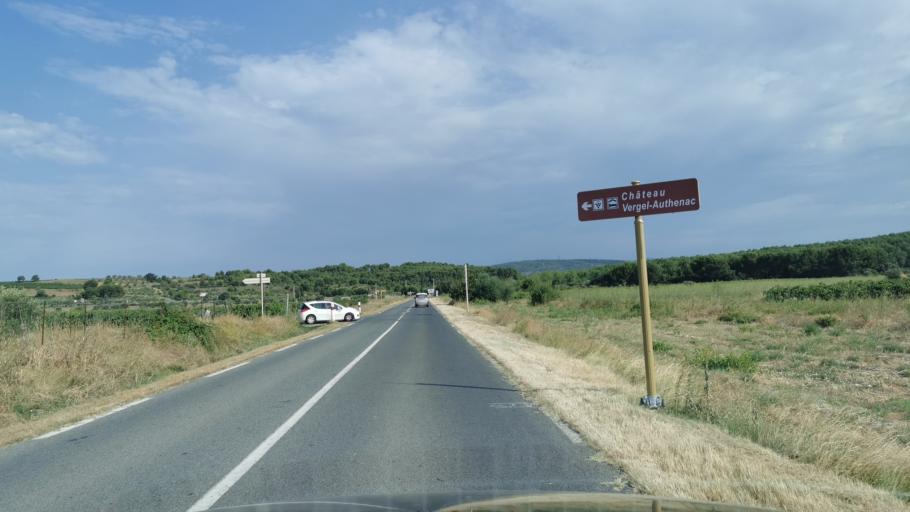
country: FR
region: Languedoc-Roussillon
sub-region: Departement de l'Aude
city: Ginestas
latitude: 43.2872
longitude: 2.8705
